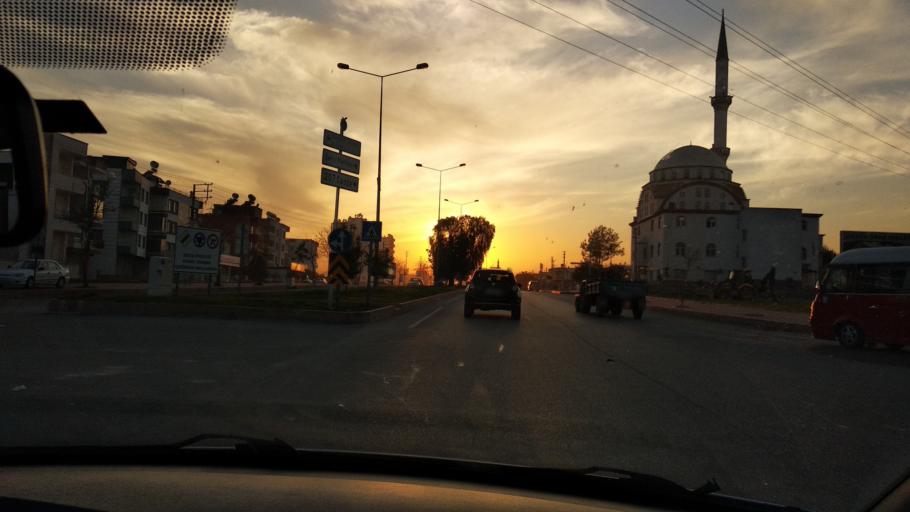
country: TR
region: Mersin
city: Mercin
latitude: 36.8309
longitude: 34.6144
